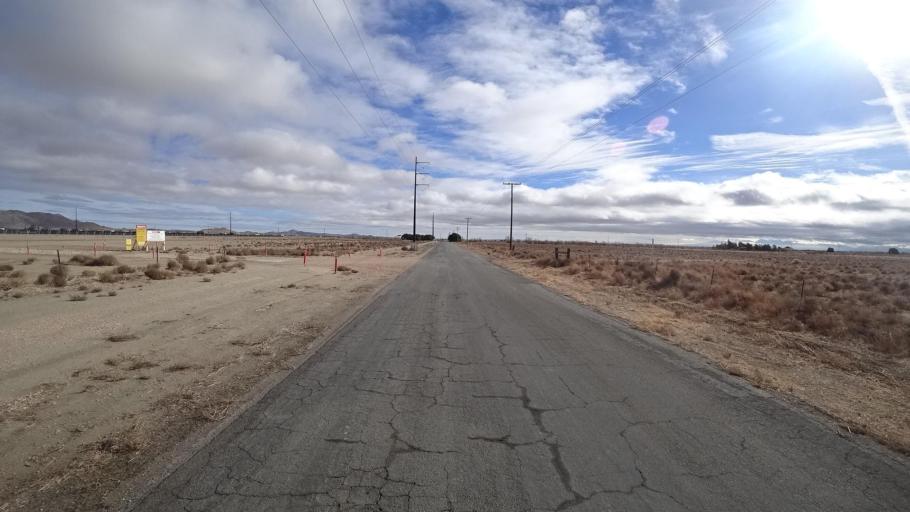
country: US
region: California
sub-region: Kern County
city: Rosamond
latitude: 34.8345
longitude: -118.3135
